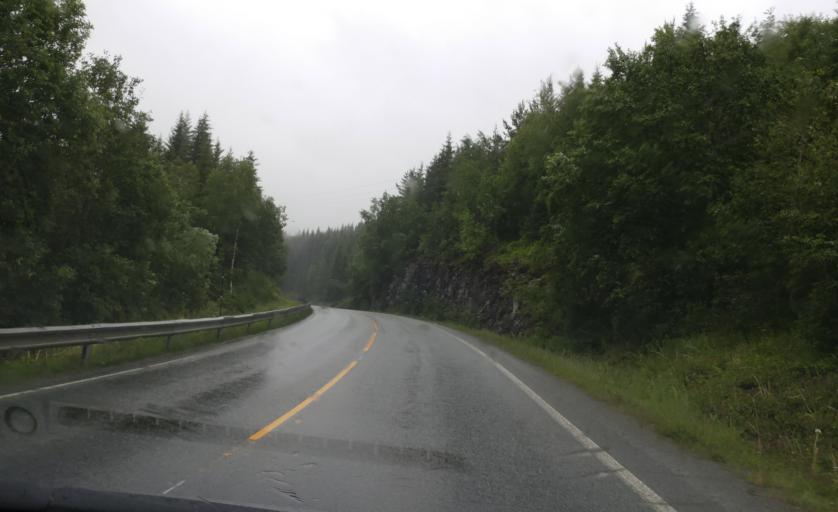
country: NO
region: Nord-Trondelag
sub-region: Stjordal
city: Stjordalshalsen
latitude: 63.3982
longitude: 10.9507
